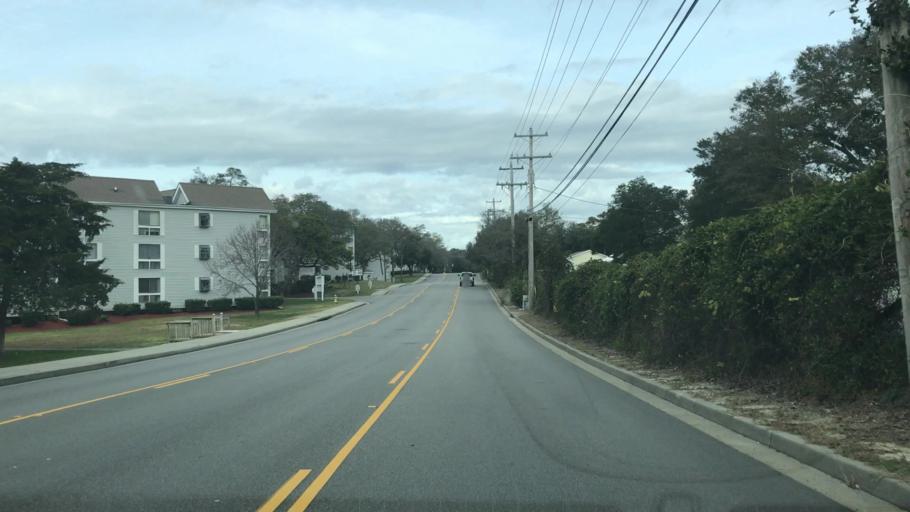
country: US
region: South Carolina
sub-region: Horry County
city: North Myrtle Beach
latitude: 33.7651
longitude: -78.7863
